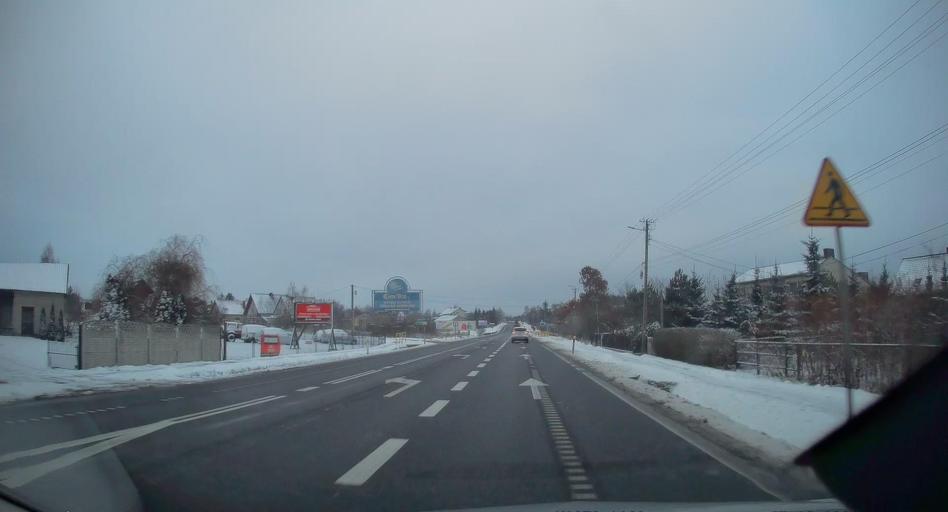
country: PL
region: Swietokrzyskie
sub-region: Powiat kielecki
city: Miedziana Gora
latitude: 50.9409
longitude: 20.5478
